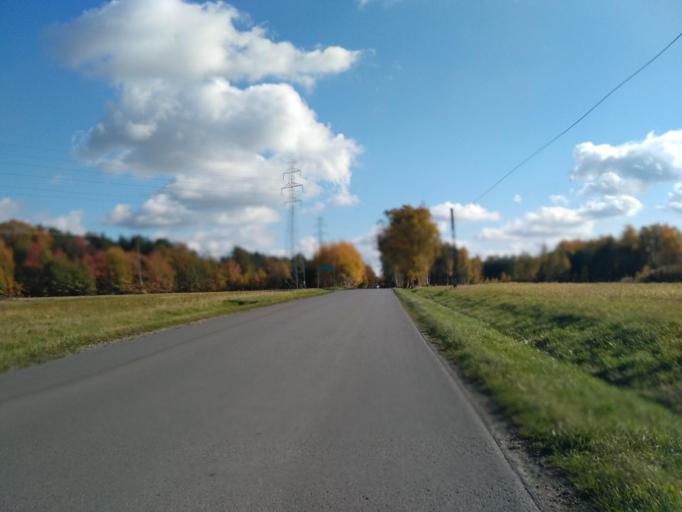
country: PL
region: Subcarpathian Voivodeship
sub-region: Powiat rzeszowski
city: Glogow Malopolski
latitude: 50.1567
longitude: 21.9210
